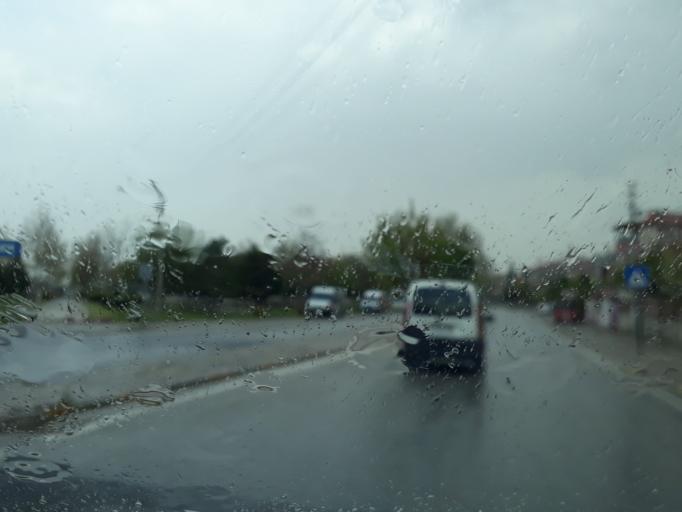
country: TR
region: Konya
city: Selcuklu
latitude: 37.9224
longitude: 32.4907
